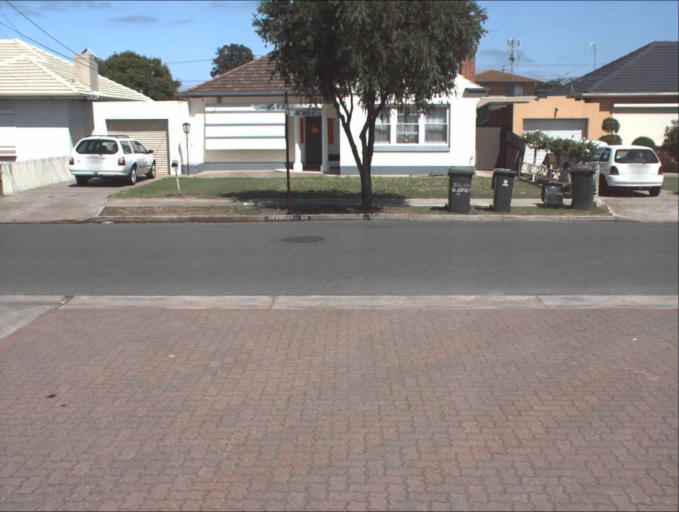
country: AU
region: South Australia
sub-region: Charles Sturt
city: Woodville
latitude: -34.8788
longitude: 138.5679
